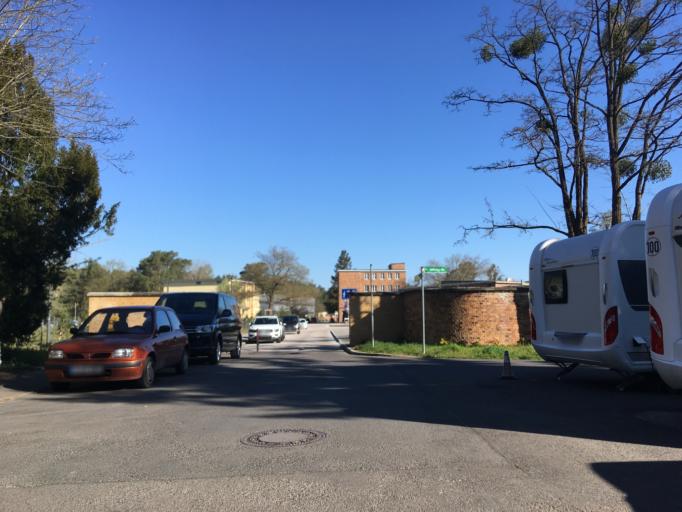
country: DE
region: Brandenburg
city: Bernau bei Berlin
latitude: 52.7052
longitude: 13.5439
